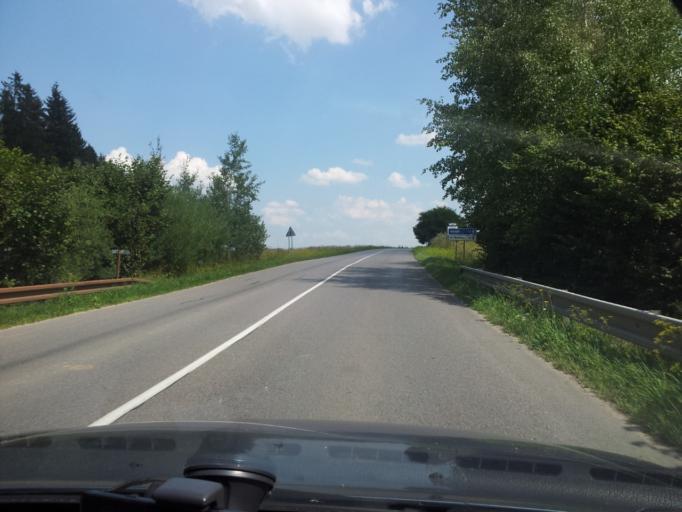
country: SK
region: Zilinsky
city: Namestovo
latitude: 49.3886
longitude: 19.4530
